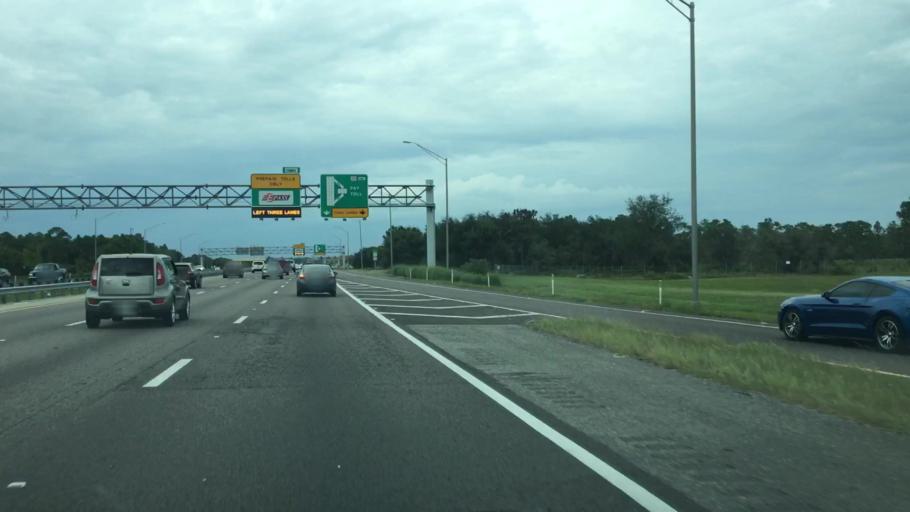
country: US
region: Florida
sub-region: Orange County
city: Azalea Park
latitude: 28.4816
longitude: -81.2403
